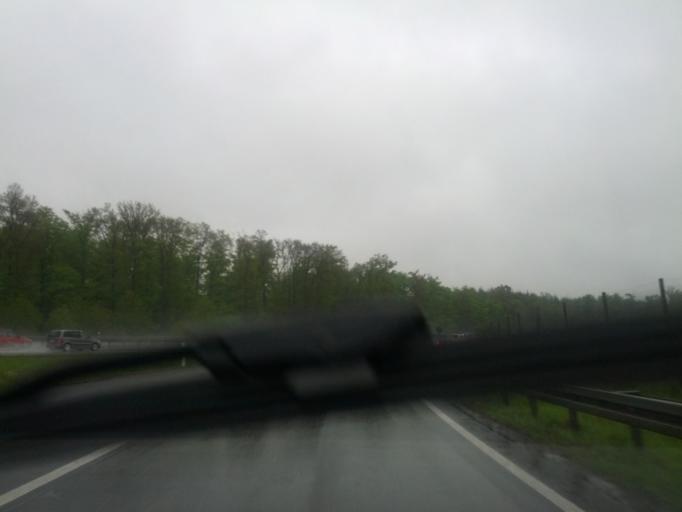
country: DE
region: Hesse
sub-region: Regierungsbezirk Giessen
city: Reiskirchen
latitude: 50.6113
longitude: 8.8311
